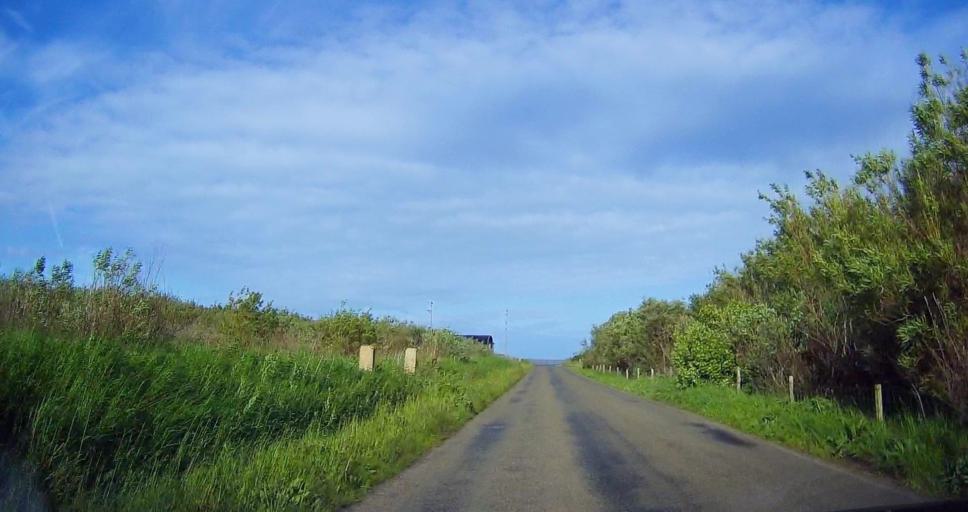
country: GB
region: Scotland
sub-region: Orkney Islands
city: Stromness
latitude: 58.8035
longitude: -3.2252
